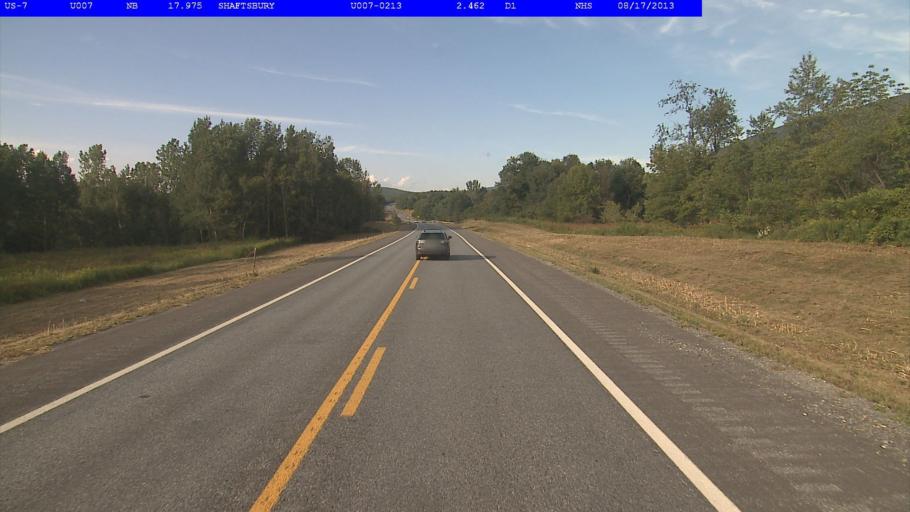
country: US
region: Vermont
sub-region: Bennington County
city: North Bennington
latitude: 42.9635
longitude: -73.1654
